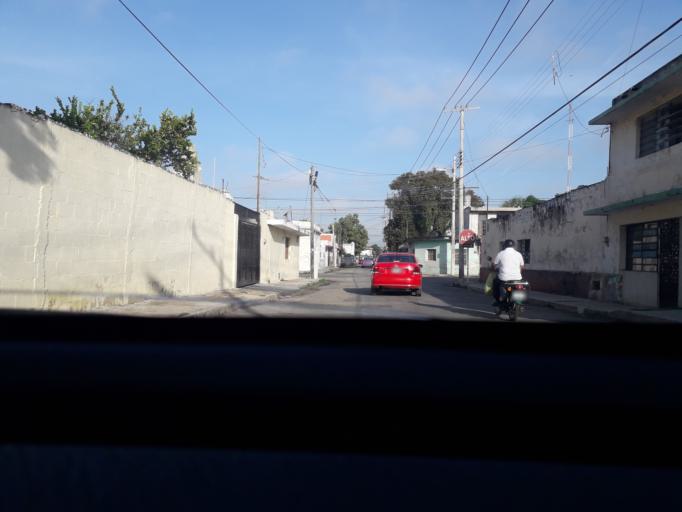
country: MX
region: Yucatan
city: Merida
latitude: 20.9607
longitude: -89.6320
